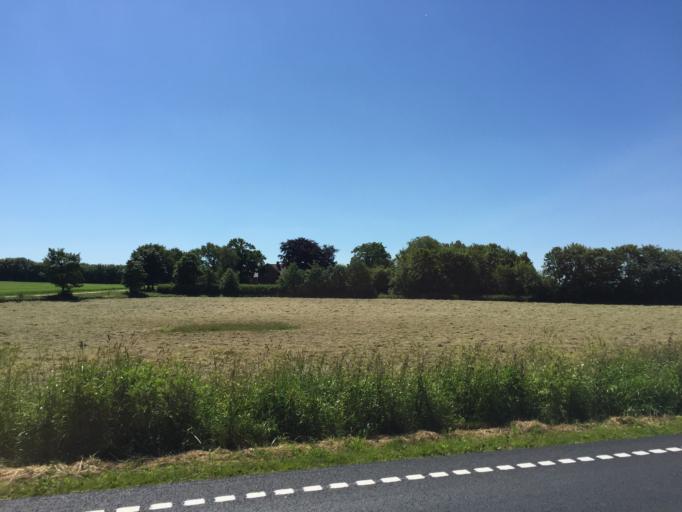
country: DK
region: South Denmark
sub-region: Aabenraa Kommune
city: Rodekro
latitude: 55.1542
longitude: 9.2506
